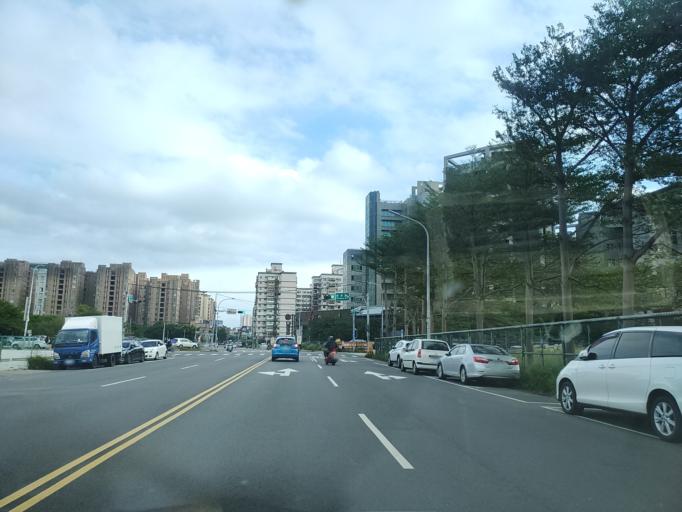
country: TW
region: Taiwan
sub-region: Hsinchu
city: Hsinchu
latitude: 24.8040
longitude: 120.9910
